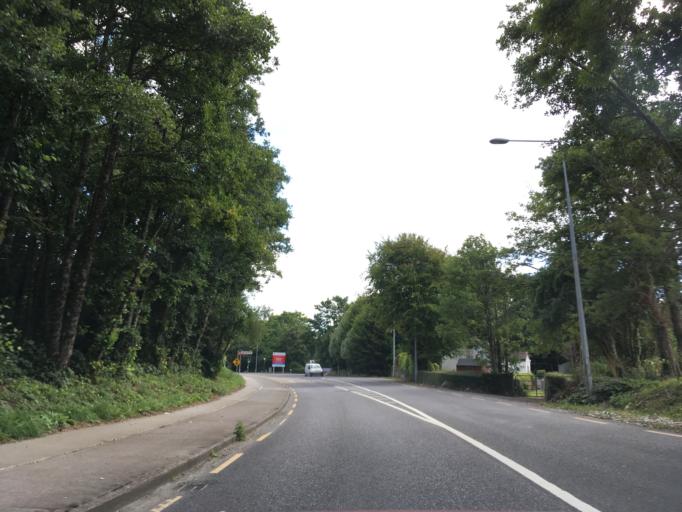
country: IE
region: Munster
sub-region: County Cork
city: Carrigaline
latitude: 51.8103
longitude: -8.3747
